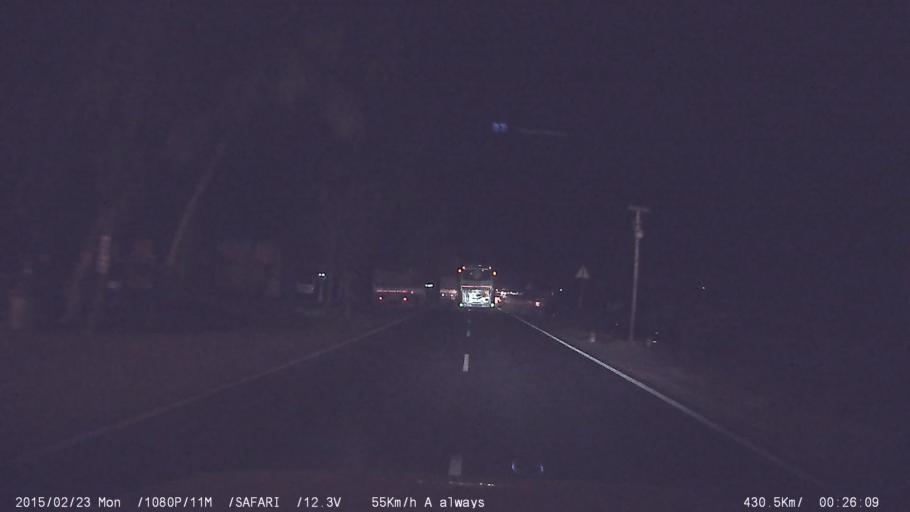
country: IN
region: Tamil Nadu
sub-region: Salem
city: Omalur
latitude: 11.9422
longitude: 78.0495
